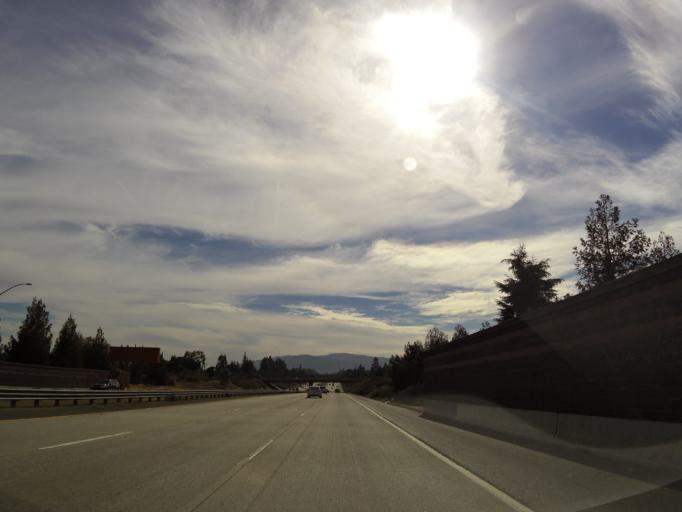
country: US
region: California
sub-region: Santa Clara County
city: Cupertino
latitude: 37.2964
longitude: -122.0280
